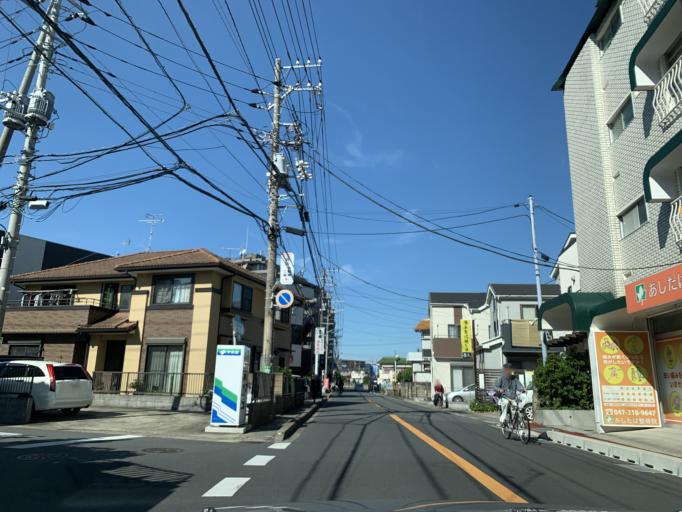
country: JP
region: Tokyo
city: Urayasu
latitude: 35.6724
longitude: 139.8930
